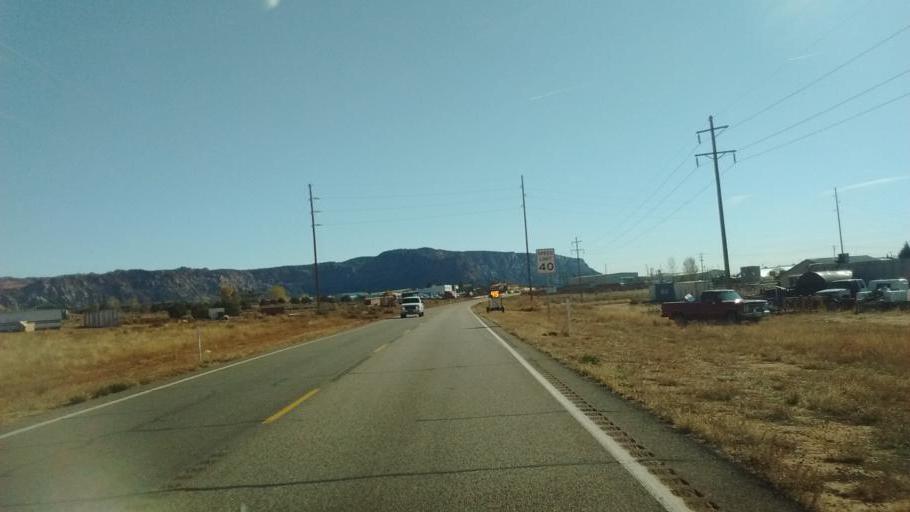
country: US
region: Arizona
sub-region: Mohave County
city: Colorado City
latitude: 37.0060
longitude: -113.0064
